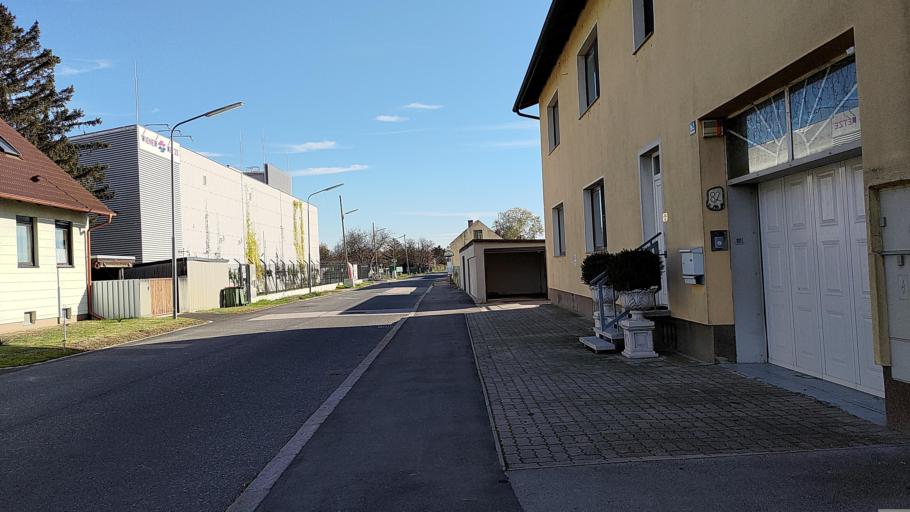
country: AT
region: Lower Austria
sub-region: Politischer Bezirk Wien-Umgebung
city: Schwechat
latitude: 48.1588
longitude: 16.4893
